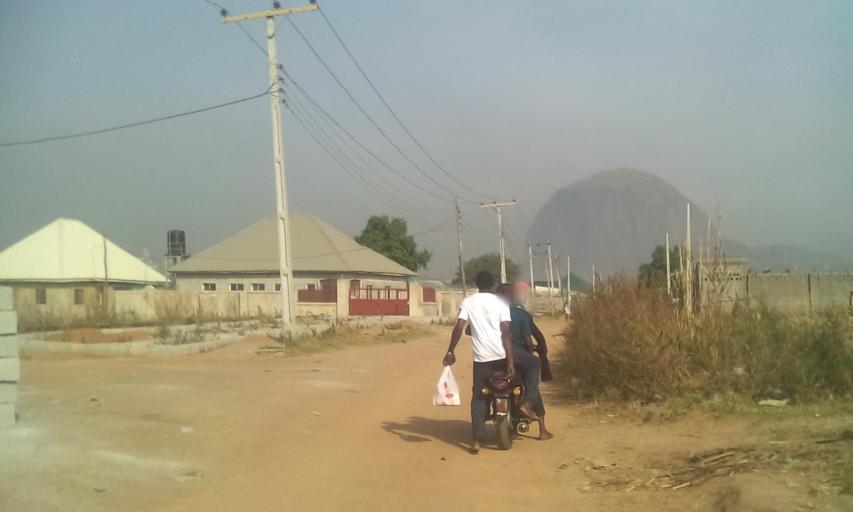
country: NG
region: Abuja Federal Capital Territory
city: Madala
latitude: 9.1062
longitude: 7.2426
